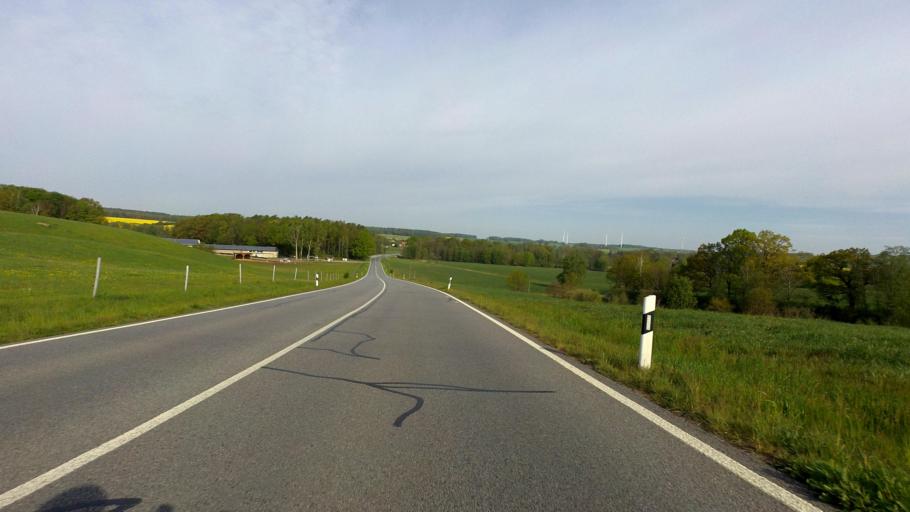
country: DE
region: Saxony
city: Stolpen
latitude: 51.0535
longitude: 14.0709
